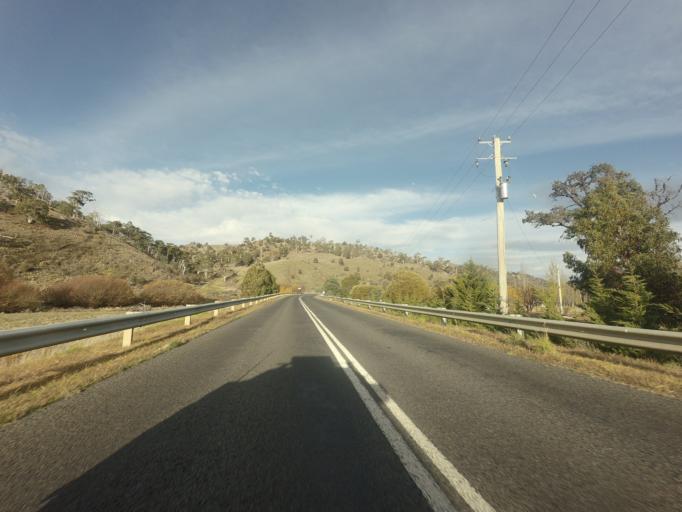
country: AU
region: Tasmania
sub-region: Brighton
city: Bridgewater
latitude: -42.4377
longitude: 147.1492
